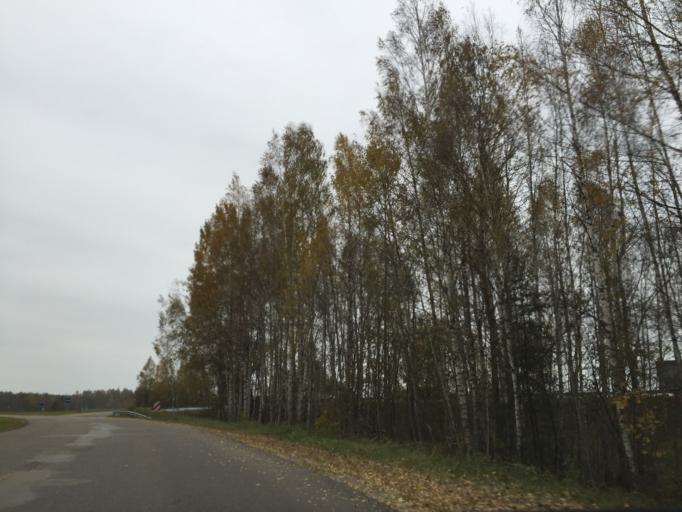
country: LV
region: Marupe
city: Marupe
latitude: 56.8366
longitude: 24.0313
